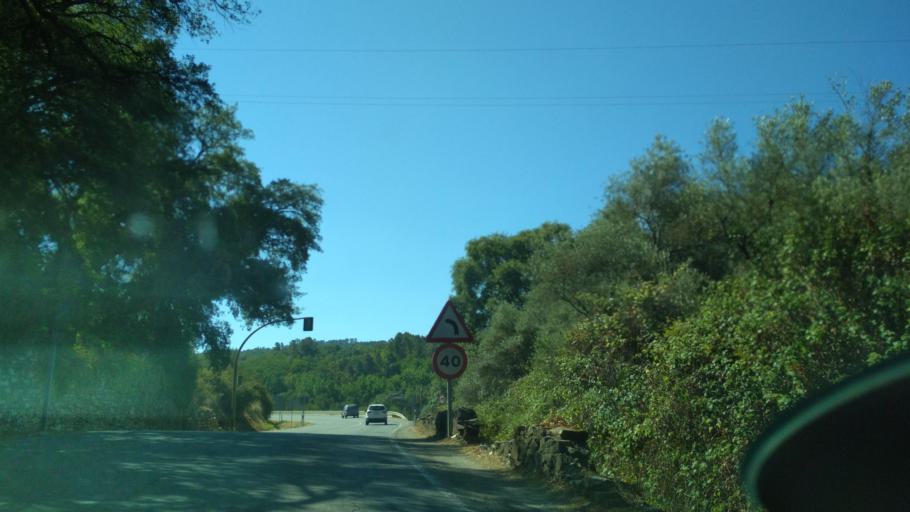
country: ES
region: Andalusia
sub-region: Provincia de Huelva
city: Galaroza
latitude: 37.9224
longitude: -6.7062
